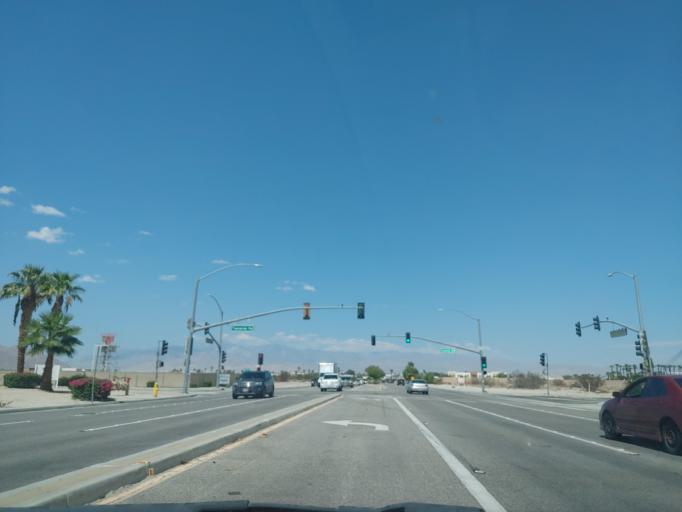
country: US
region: California
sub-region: Riverside County
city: Palm Springs
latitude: 33.8335
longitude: -116.5039
